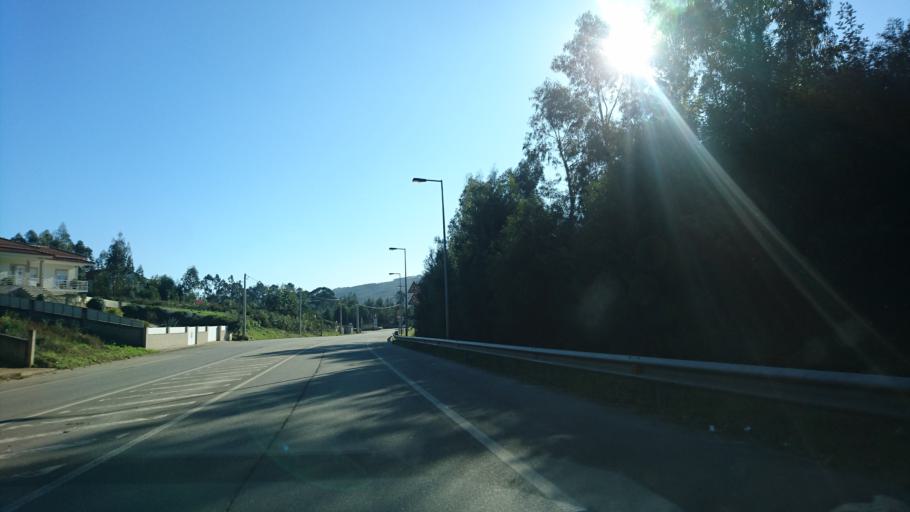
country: PT
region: Porto
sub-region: Paredes
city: Recarei
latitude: 41.1507
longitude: -8.3948
